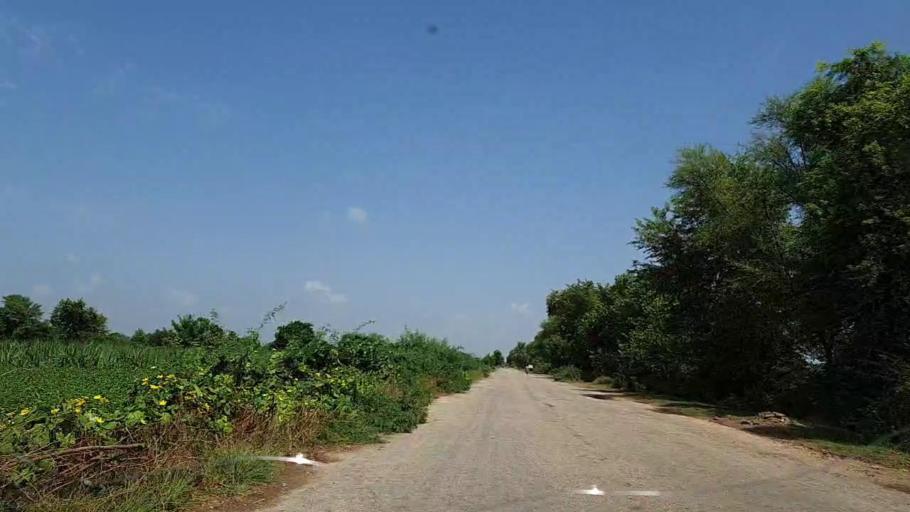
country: PK
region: Sindh
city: Pad Idan
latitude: 26.8038
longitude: 68.2167
